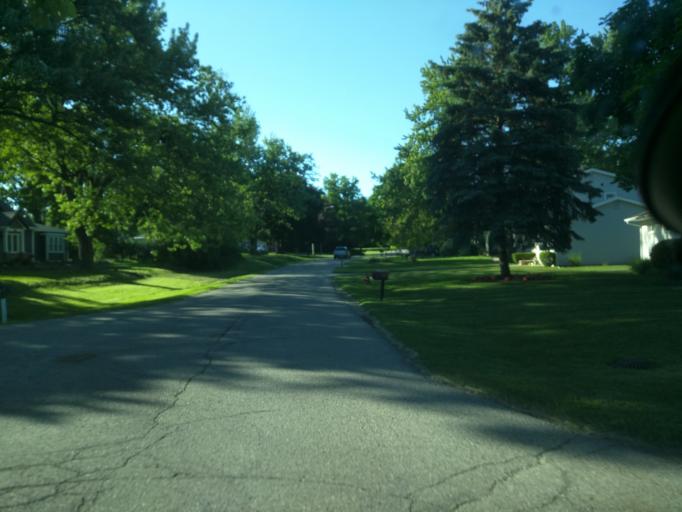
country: US
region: Michigan
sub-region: Ingham County
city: Edgemont Park
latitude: 42.7421
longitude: -84.5946
